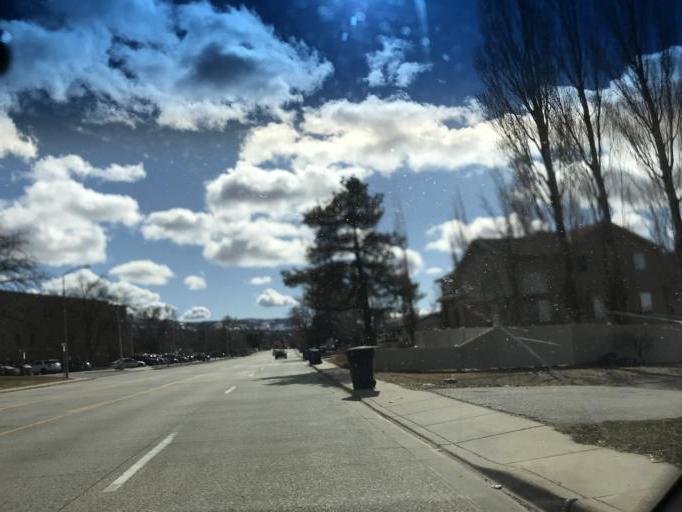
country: US
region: Utah
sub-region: Davis County
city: Bountiful
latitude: 40.8824
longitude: -111.8725
